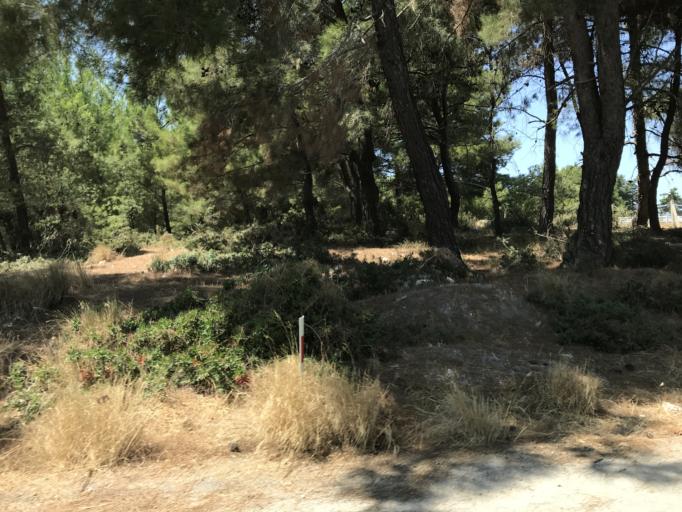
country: TR
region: Izmir
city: Urla
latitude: 38.2844
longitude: 26.7273
